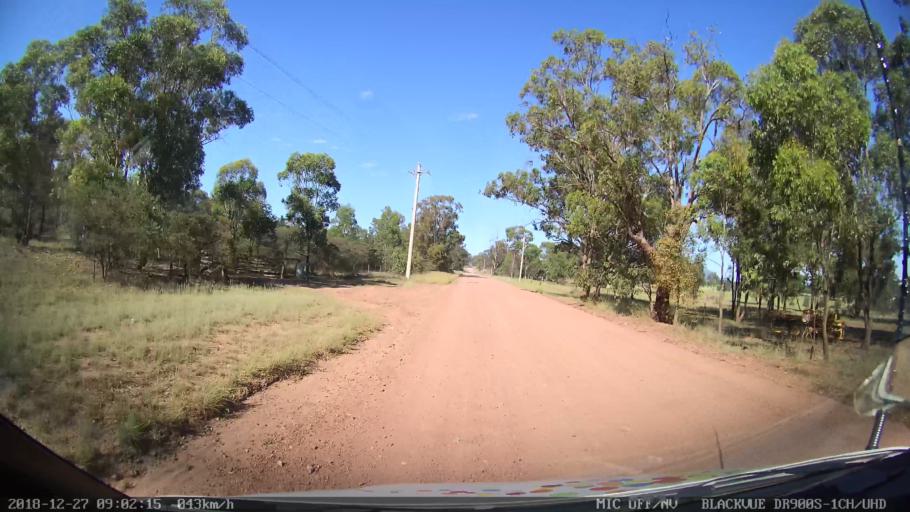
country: AU
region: New South Wales
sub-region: Lithgow
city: Portland
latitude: -33.1021
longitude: 150.2106
